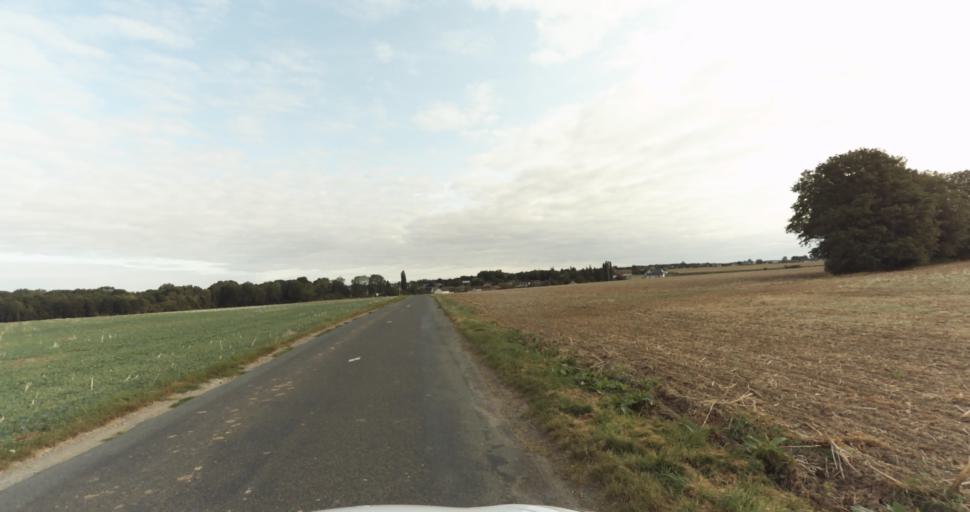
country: FR
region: Haute-Normandie
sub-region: Departement de l'Eure
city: Saint-Germain-sur-Avre
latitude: 48.8133
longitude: 1.2662
